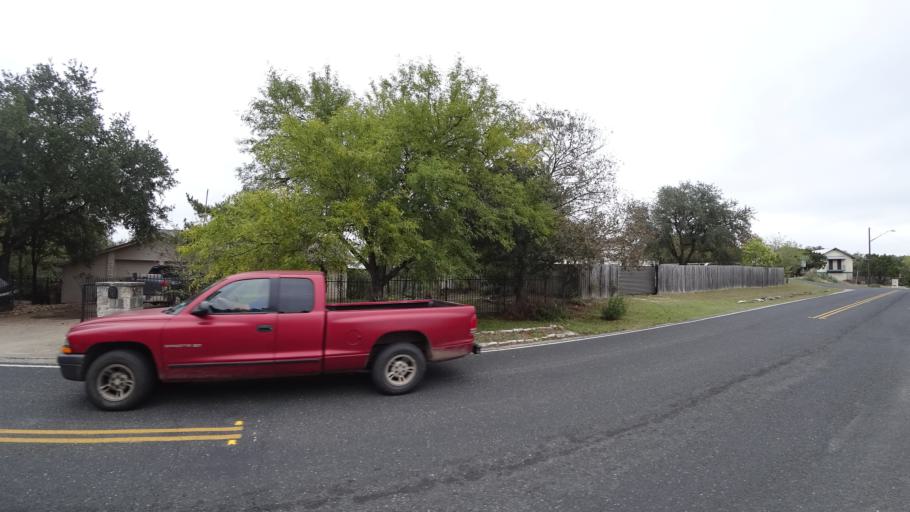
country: US
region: Texas
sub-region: Travis County
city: Barton Creek
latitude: 30.2418
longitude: -97.8917
